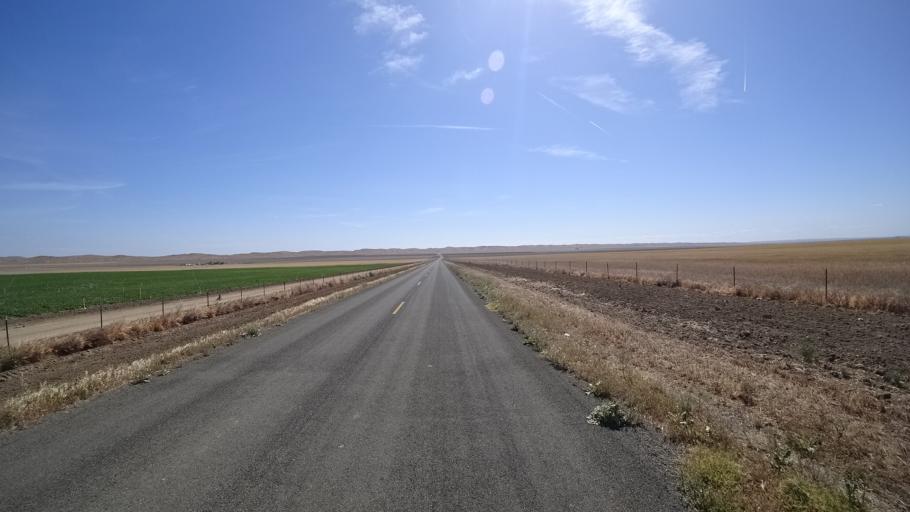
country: US
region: California
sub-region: Kings County
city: Avenal
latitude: 35.9351
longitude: -120.0700
